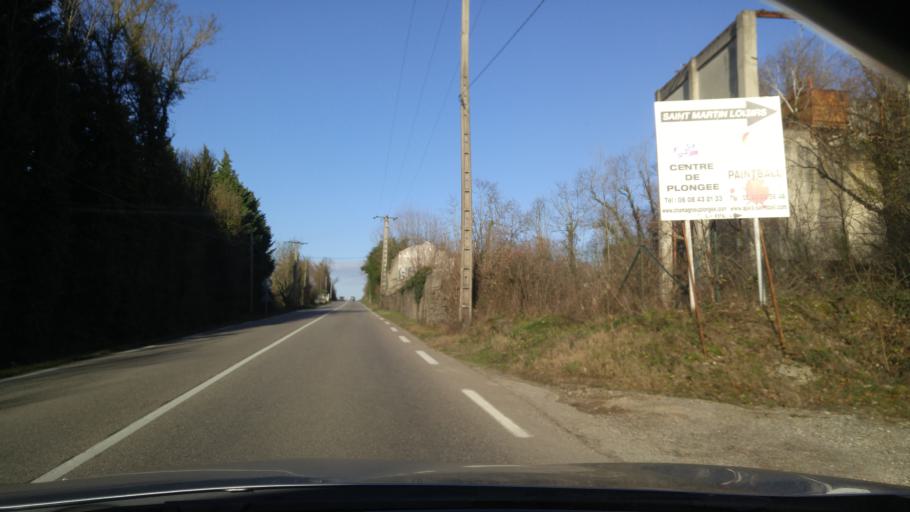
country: FR
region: Rhone-Alpes
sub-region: Departement de l'Isere
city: Chamagnieu
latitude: 45.6835
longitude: 5.1725
